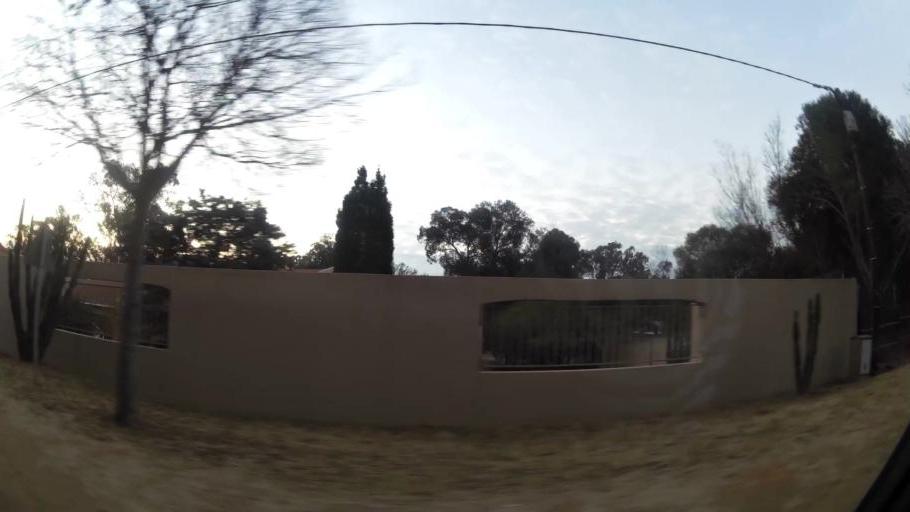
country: ZA
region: Gauteng
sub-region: City of Johannesburg Metropolitan Municipality
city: Midrand
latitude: -25.9794
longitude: 28.0754
